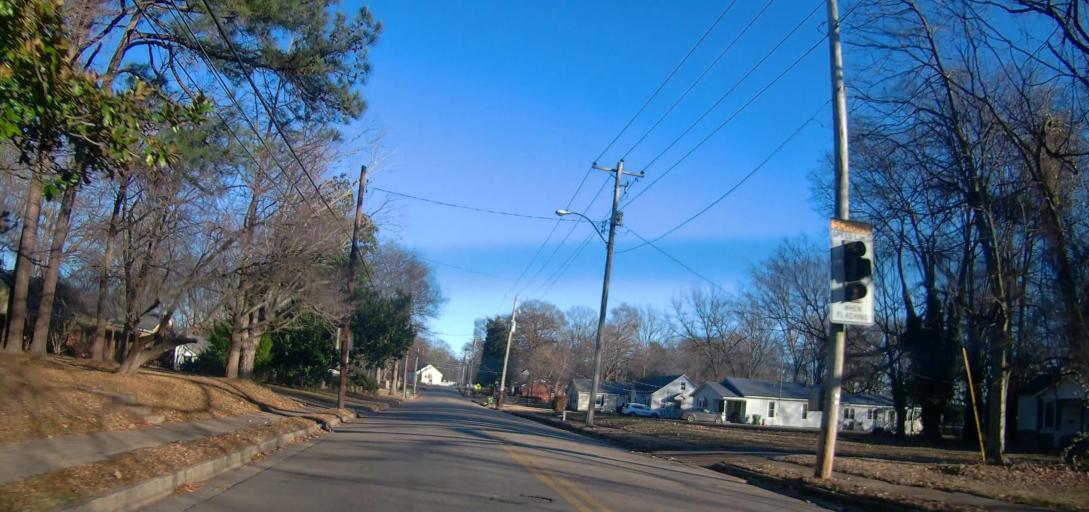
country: US
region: Tennessee
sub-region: Shelby County
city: Millington
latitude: 35.3503
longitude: -89.8991
